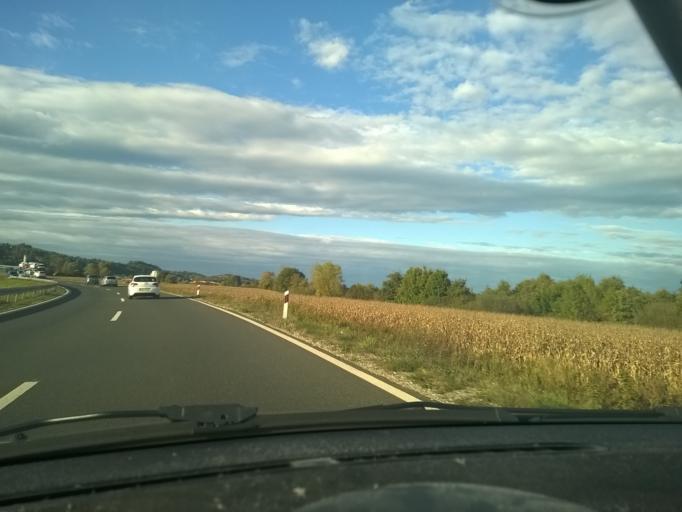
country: HR
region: Zagrebacka
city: Pojatno
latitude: 45.9005
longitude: 15.8156
